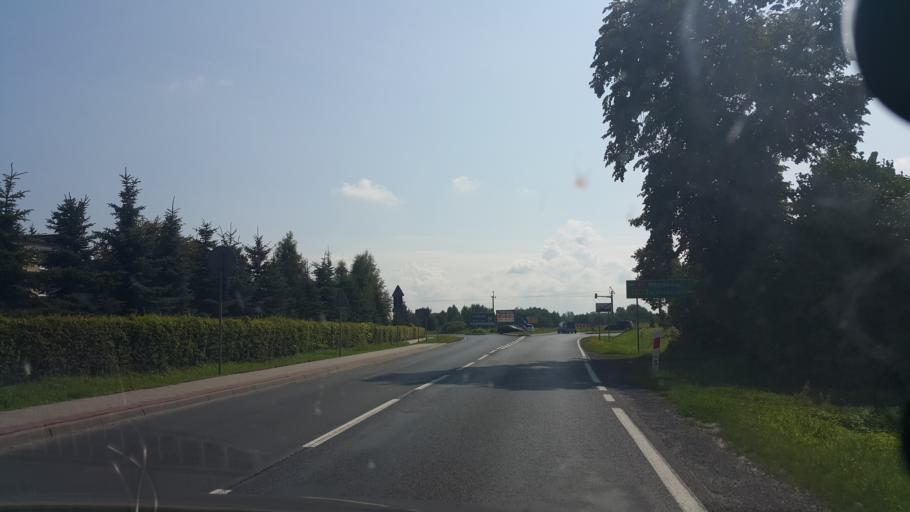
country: PL
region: Lublin Voivodeship
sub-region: Powiat leczynski
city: Cycow
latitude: 51.2890
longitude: 23.1052
